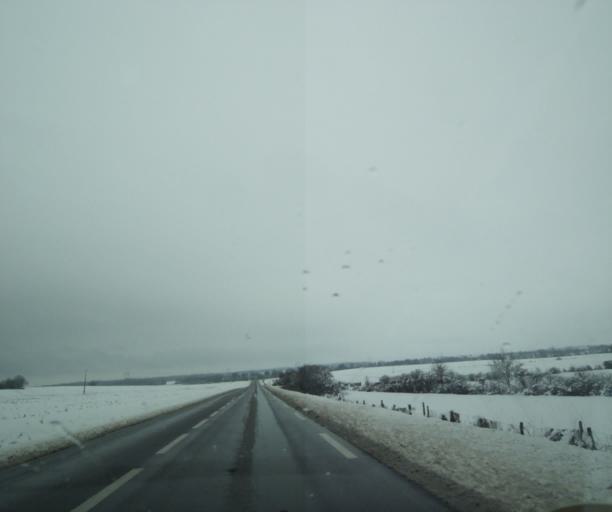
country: FR
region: Champagne-Ardenne
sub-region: Departement de la Haute-Marne
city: Montier-en-Der
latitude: 48.5153
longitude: 4.8067
